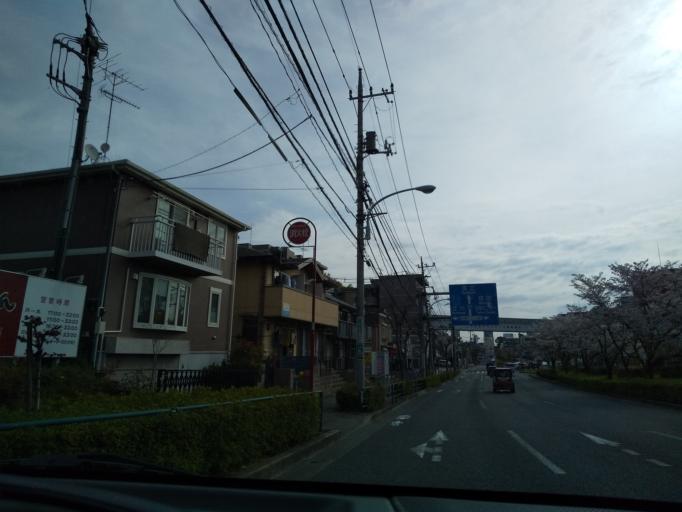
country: JP
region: Tokyo
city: Hino
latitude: 35.6371
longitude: 139.4143
